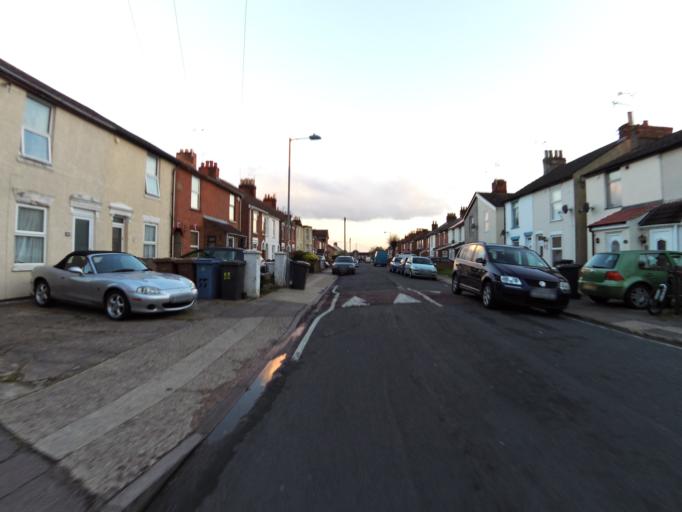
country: GB
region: England
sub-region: Suffolk
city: Ipswich
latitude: 52.0547
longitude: 1.1843
